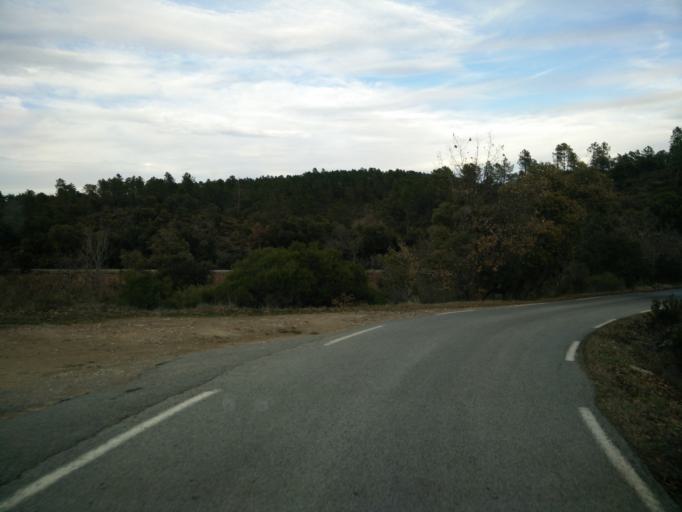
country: FR
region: Provence-Alpes-Cote d'Azur
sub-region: Departement du Var
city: Vidauban
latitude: 43.3867
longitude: 6.4836
